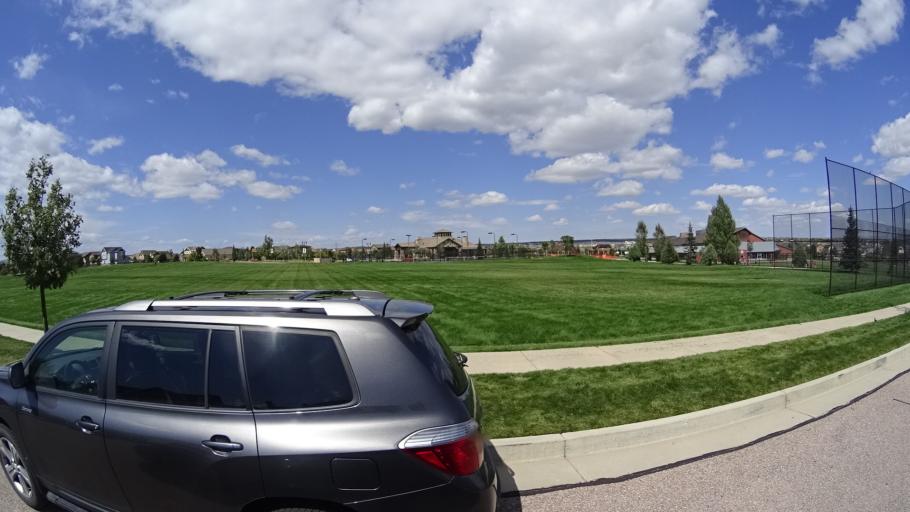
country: US
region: Colorado
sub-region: El Paso County
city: Cimarron Hills
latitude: 38.9313
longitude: -104.6766
